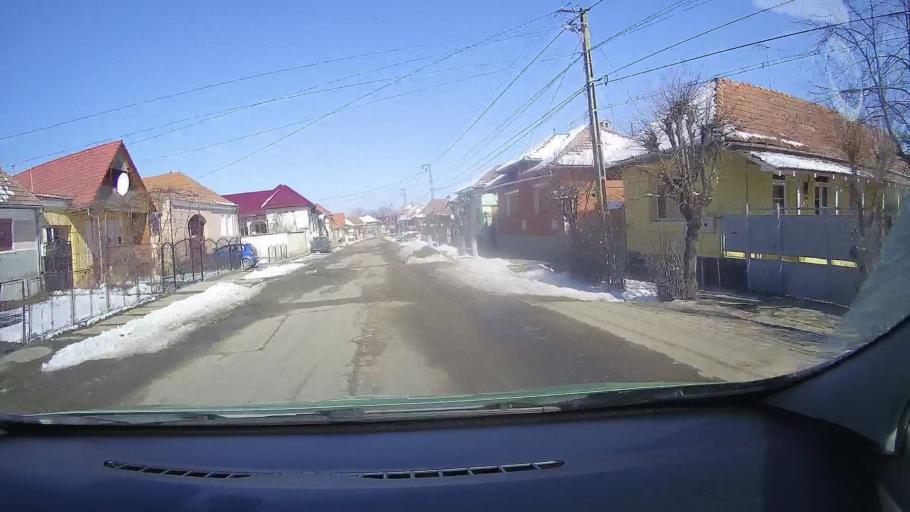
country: RO
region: Brasov
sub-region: Comuna Mandra
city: Mandra
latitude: 45.8210
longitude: 25.0056
